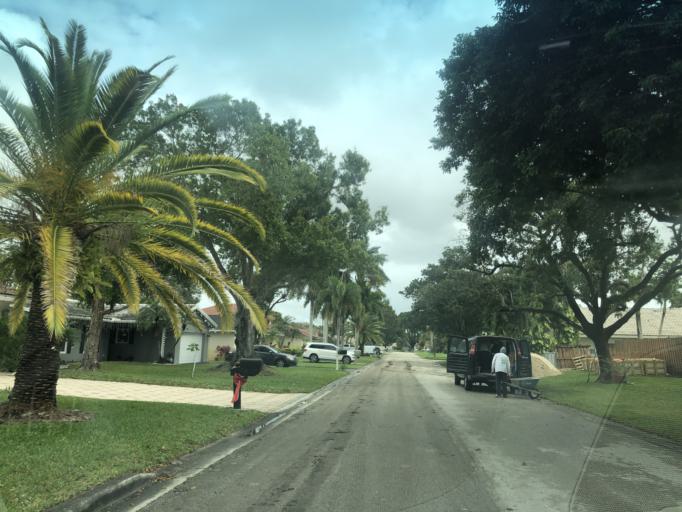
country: US
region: Florida
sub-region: Broward County
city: Coral Springs
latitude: 26.2548
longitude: -80.2459
